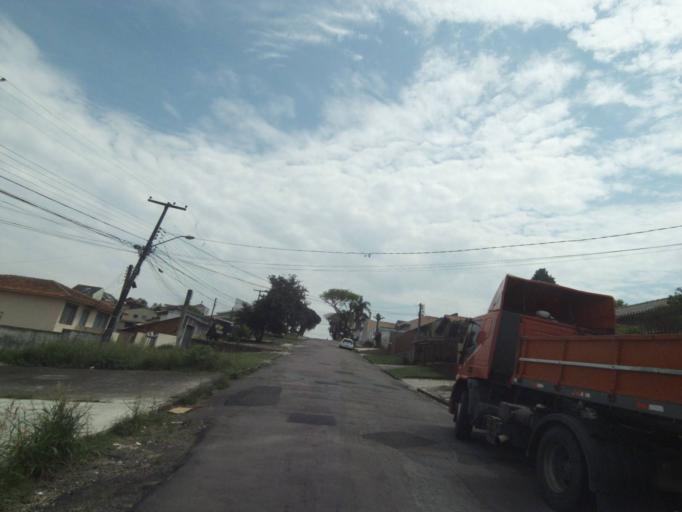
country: BR
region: Parana
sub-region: Pinhais
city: Pinhais
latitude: -25.3978
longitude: -49.2093
